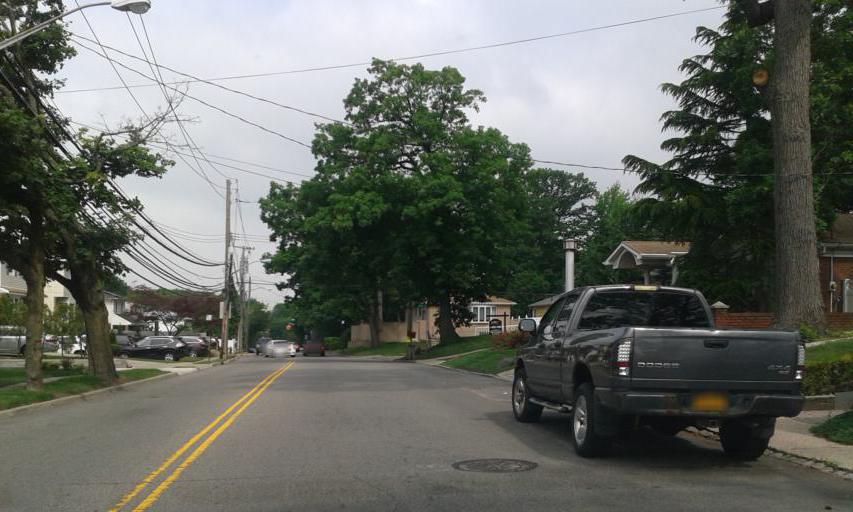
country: US
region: New York
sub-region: Richmond County
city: Staten Island
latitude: 40.5658
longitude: -74.1358
